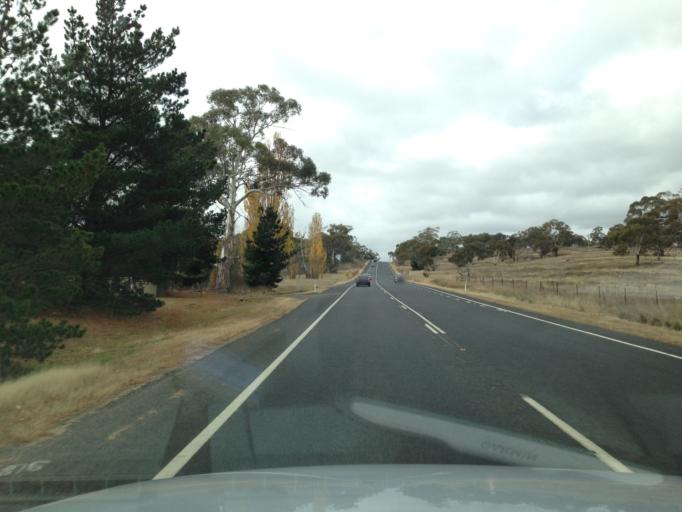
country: AU
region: New South Wales
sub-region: Cooma-Monaro
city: Cooma
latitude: -36.2409
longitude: 149.0683
